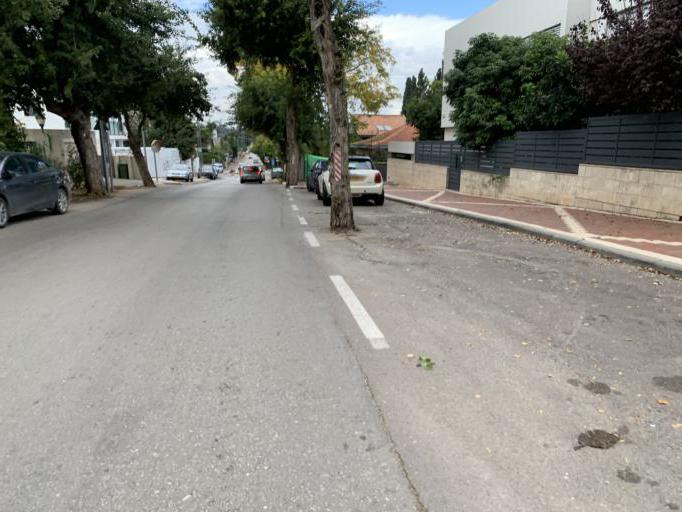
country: IL
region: Central District
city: Hod HaSharon
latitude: 32.1578
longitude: 34.8870
